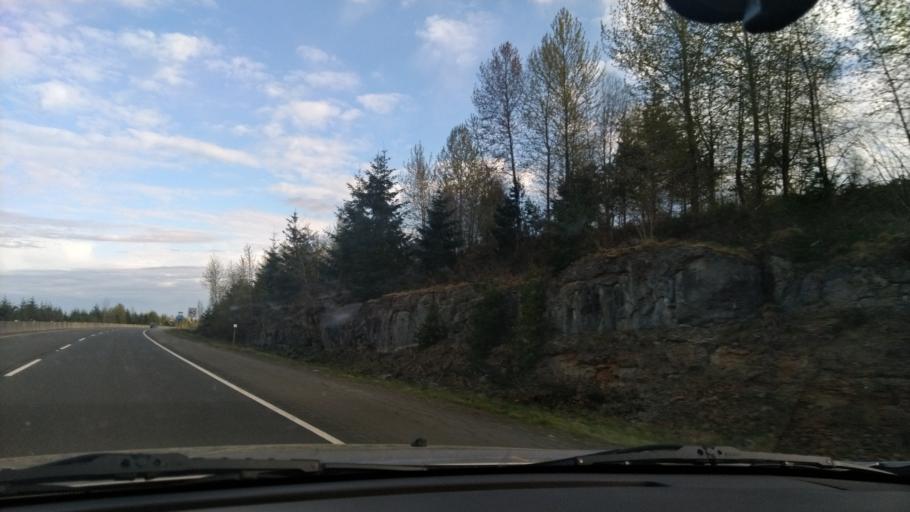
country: CA
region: British Columbia
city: Campbell River
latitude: 49.8143
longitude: -125.1762
